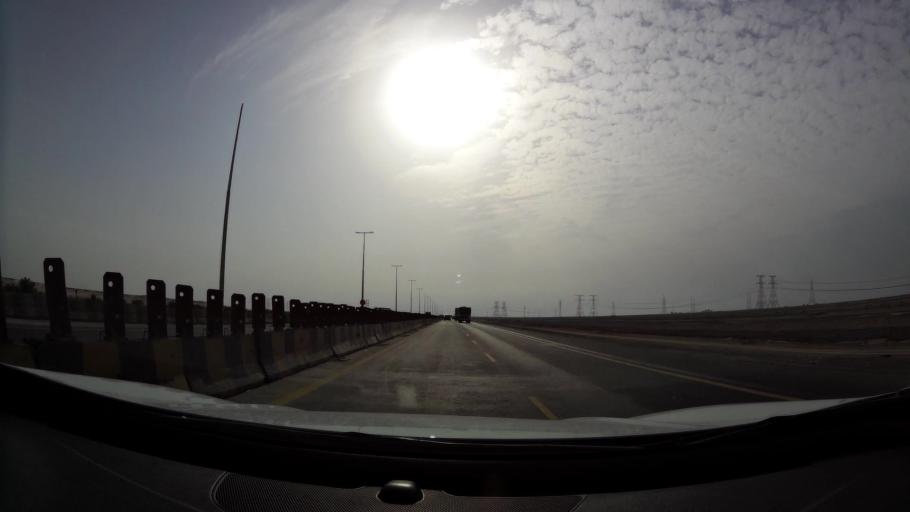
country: AE
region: Abu Dhabi
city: Abu Dhabi
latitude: 24.2266
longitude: 54.4444
